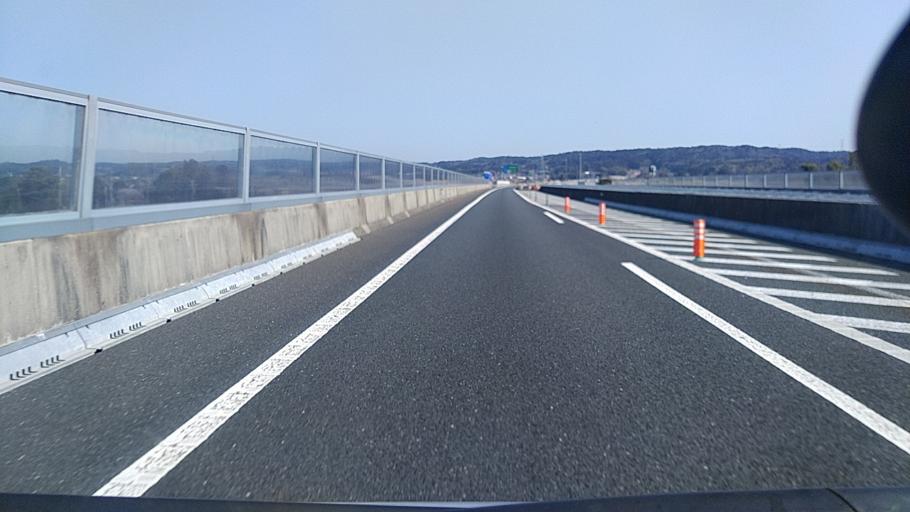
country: JP
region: Chiba
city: Kisarazu
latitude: 35.3584
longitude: 140.0412
